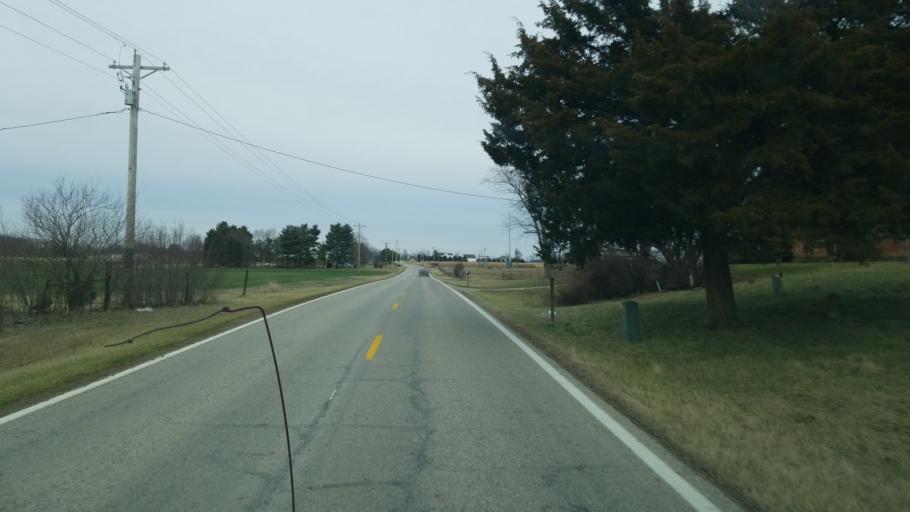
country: US
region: Ohio
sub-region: Pickaway County
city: Williamsport
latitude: 39.5673
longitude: -83.0686
